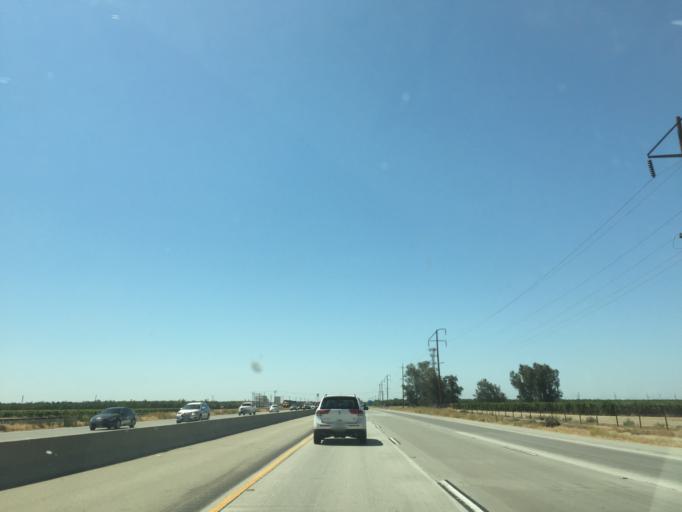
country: US
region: California
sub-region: Kern County
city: Rosedale
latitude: 35.4878
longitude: -119.1485
